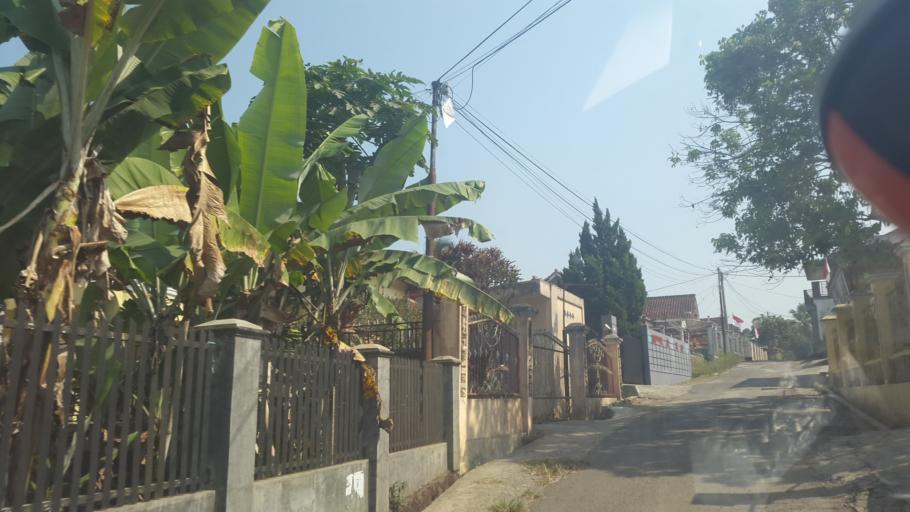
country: ID
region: West Java
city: Sukabumi
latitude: -6.8950
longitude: 106.8448
